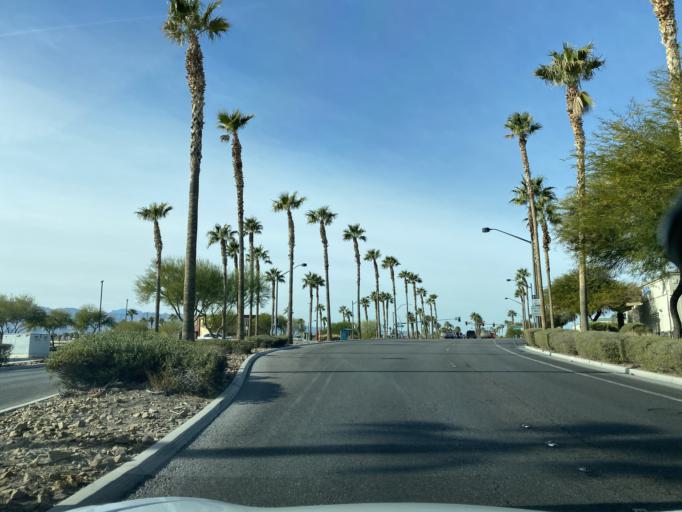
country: US
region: Nevada
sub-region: Clark County
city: Las Vegas
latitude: 36.2707
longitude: -115.2630
